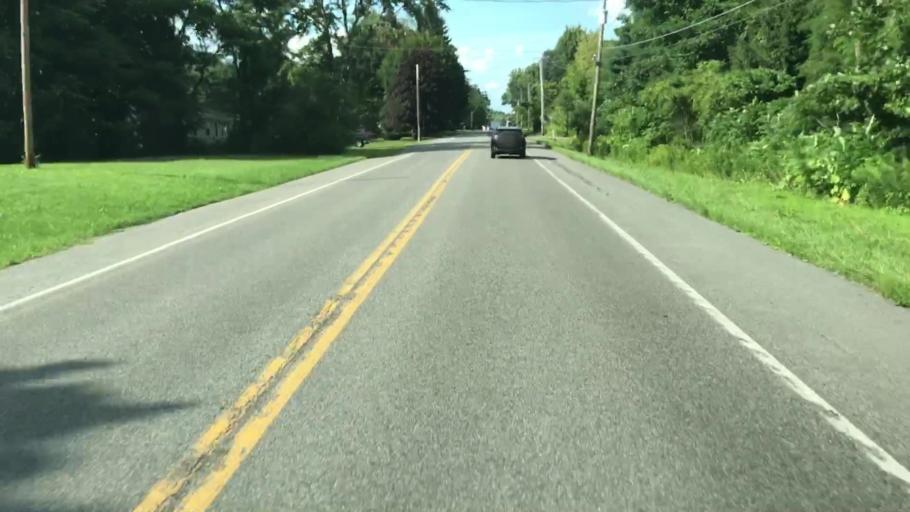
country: US
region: New York
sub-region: Onondaga County
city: Liverpool
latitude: 43.1788
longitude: -76.1992
